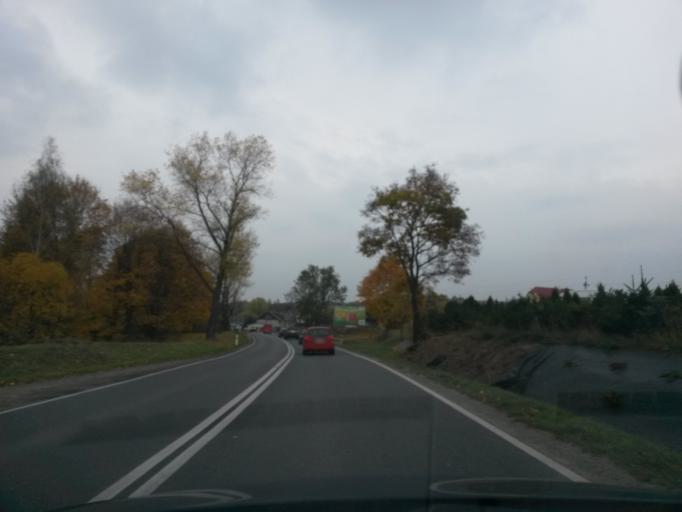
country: PL
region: Lower Silesian Voivodeship
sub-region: Powiat klodzki
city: Klodzko
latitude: 50.4178
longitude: 16.6604
